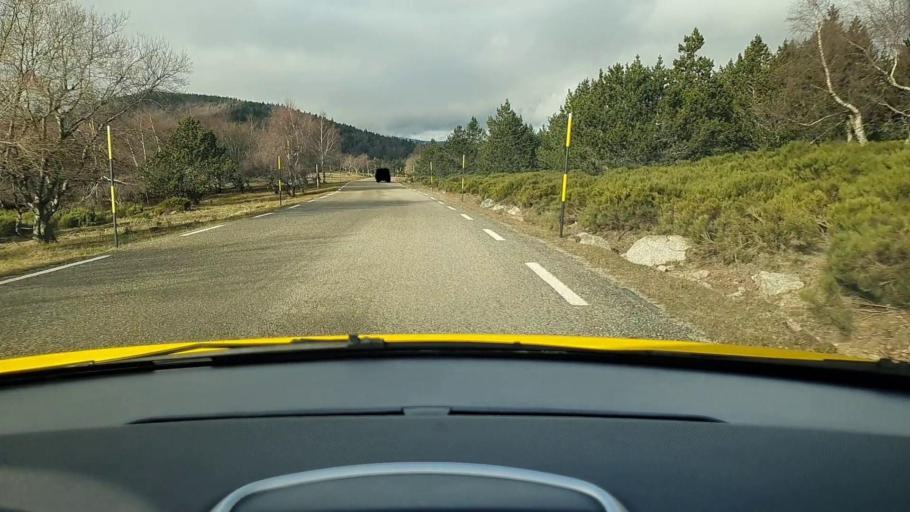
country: FR
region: Languedoc-Roussillon
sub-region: Departement du Gard
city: Branoux-les-Taillades
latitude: 44.3881
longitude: 3.8984
